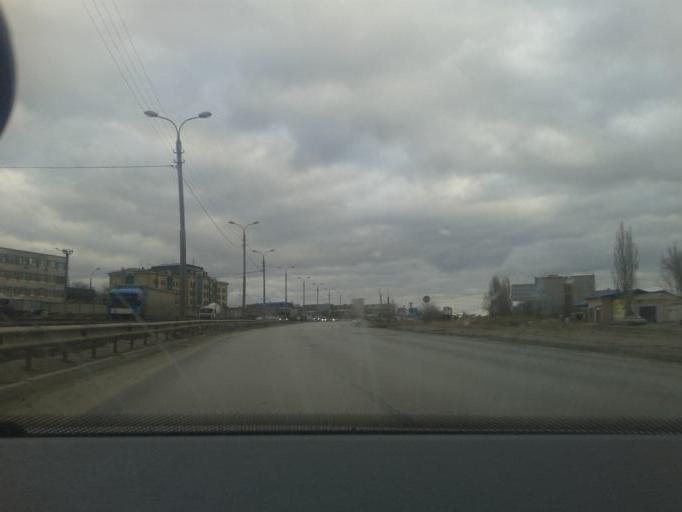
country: RU
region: Volgograd
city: Volgograd
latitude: 48.7493
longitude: 44.4694
